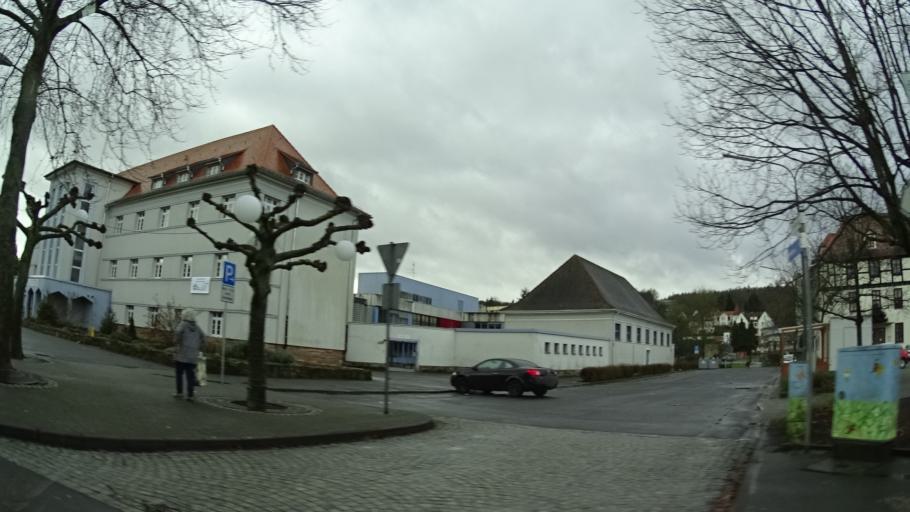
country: DE
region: Hesse
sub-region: Regierungsbezirk Darmstadt
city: Schluchtern
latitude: 50.3481
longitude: 9.5218
